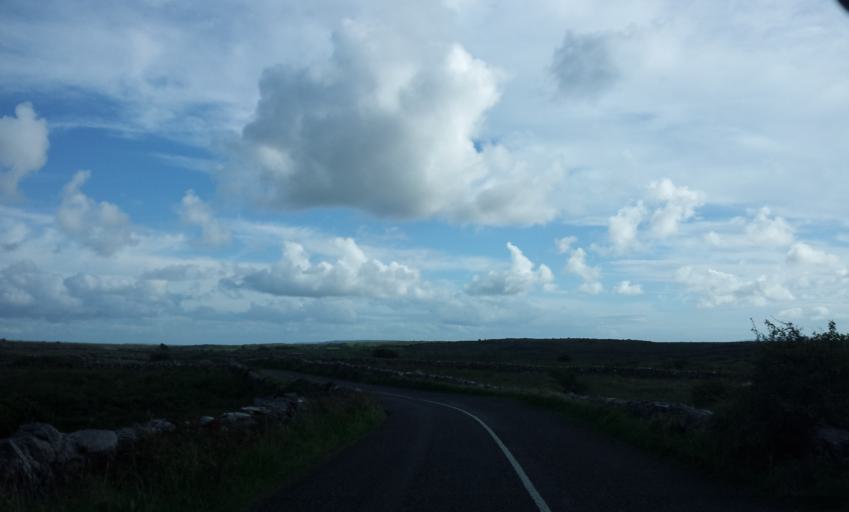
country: IE
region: Connaught
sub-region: County Galway
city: Bearna
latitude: 53.0607
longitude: -9.1490
